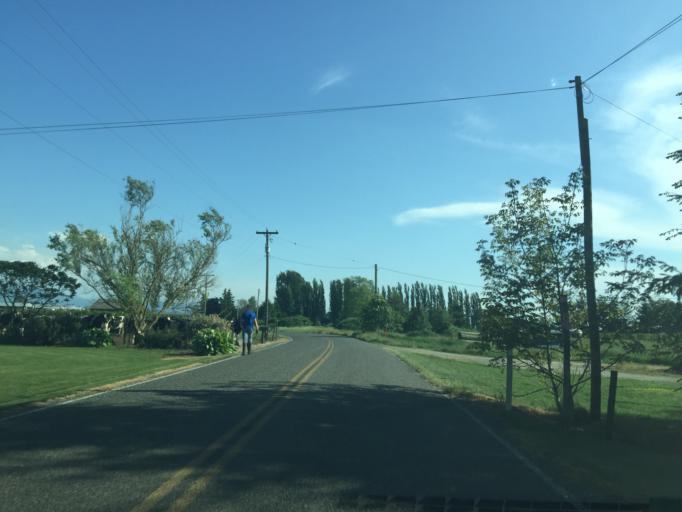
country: US
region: Washington
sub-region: Whatcom County
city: Lynden
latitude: 48.9948
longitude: -122.4631
